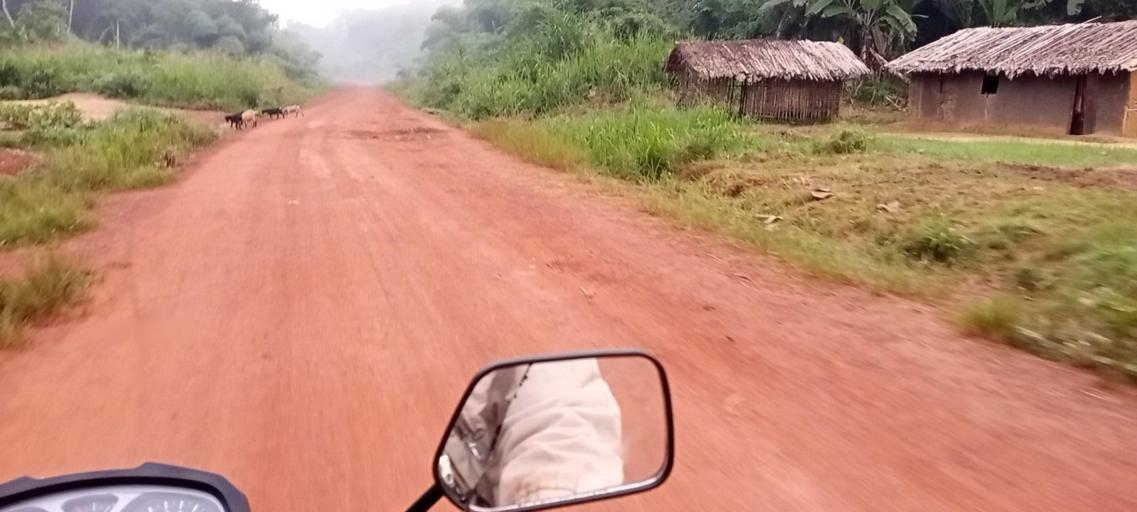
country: CD
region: Eastern Province
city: Kisangani
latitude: -0.0923
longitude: 25.6120
